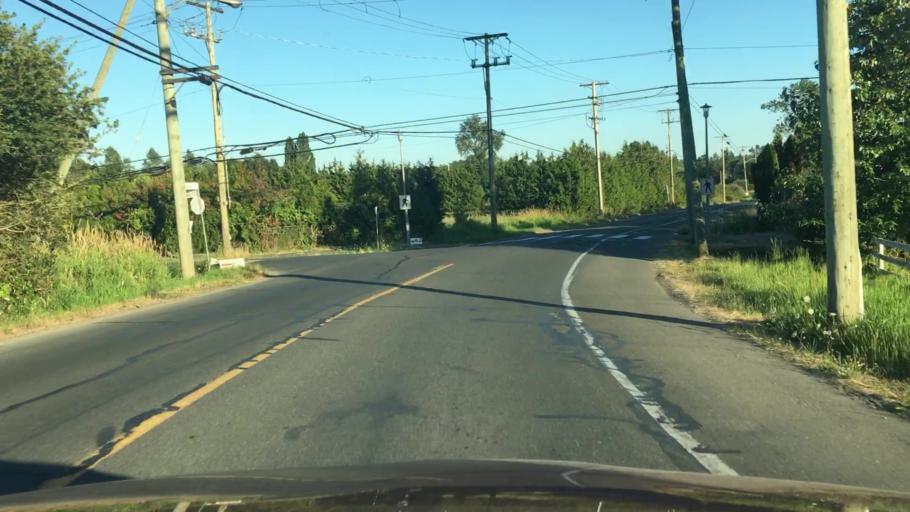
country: CA
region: British Columbia
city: Victoria
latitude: 48.4772
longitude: -123.3529
